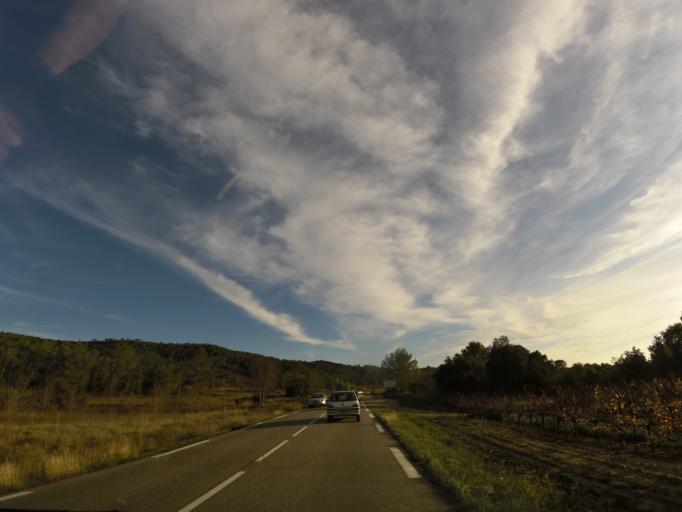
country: FR
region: Languedoc-Roussillon
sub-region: Departement du Gard
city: Ledignan
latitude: 43.9156
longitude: 4.1090
